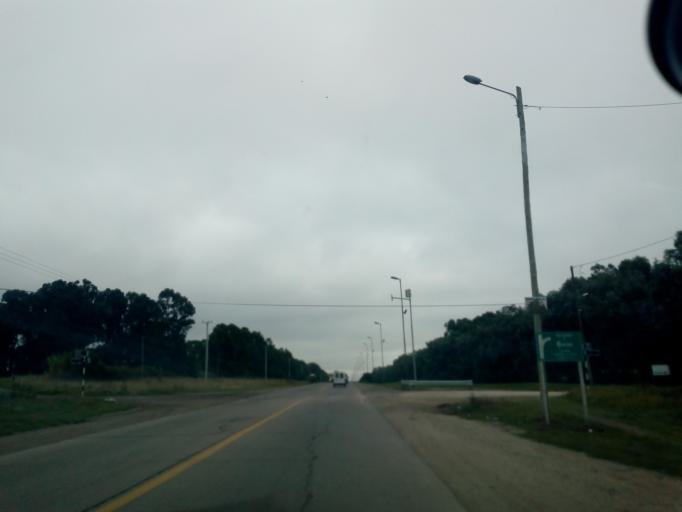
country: AR
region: Buenos Aires
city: Mar del Plata
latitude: -38.0725
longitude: -57.5756
